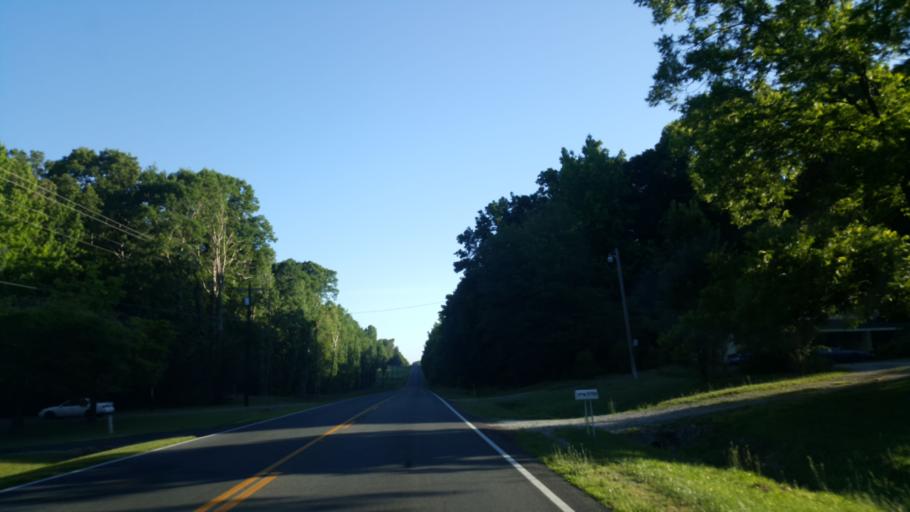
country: US
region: Tennessee
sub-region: Henderson County
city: Lexington
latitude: 35.5317
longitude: -88.3823
